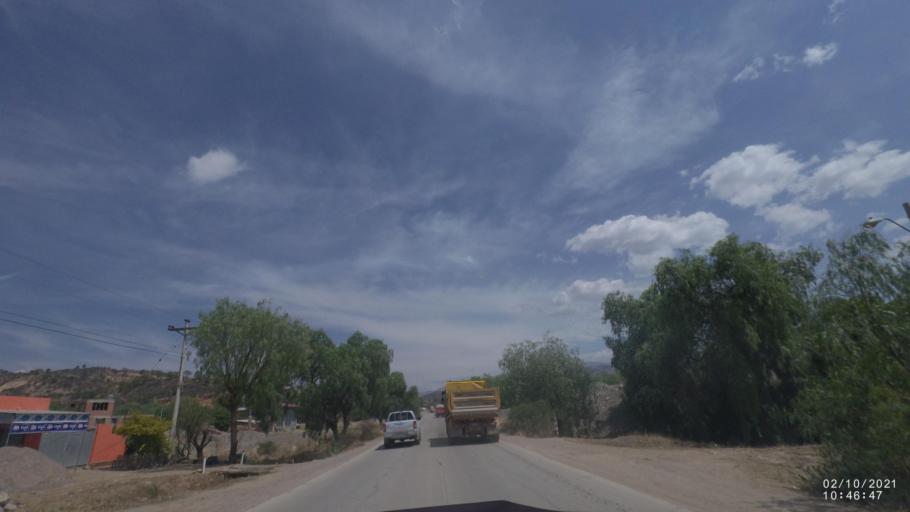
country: BO
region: Cochabamba
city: Capinota
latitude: -17.5845
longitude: -66.3256
